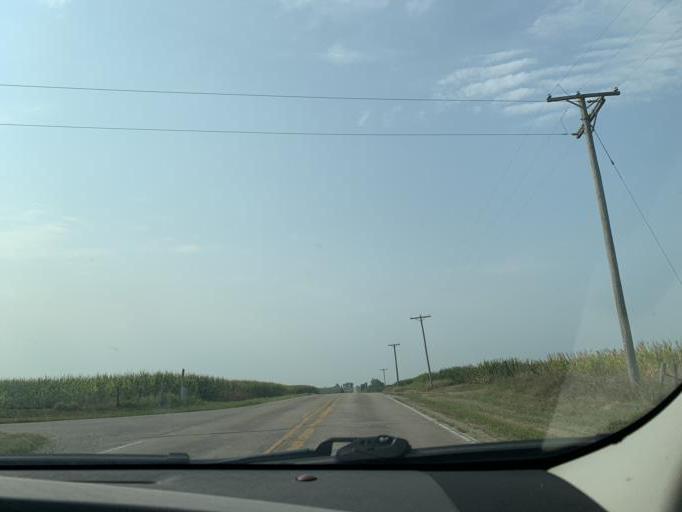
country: US
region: Illinois
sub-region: Whiteside County
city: Morrison
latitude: 41.8699
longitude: -89.9204
